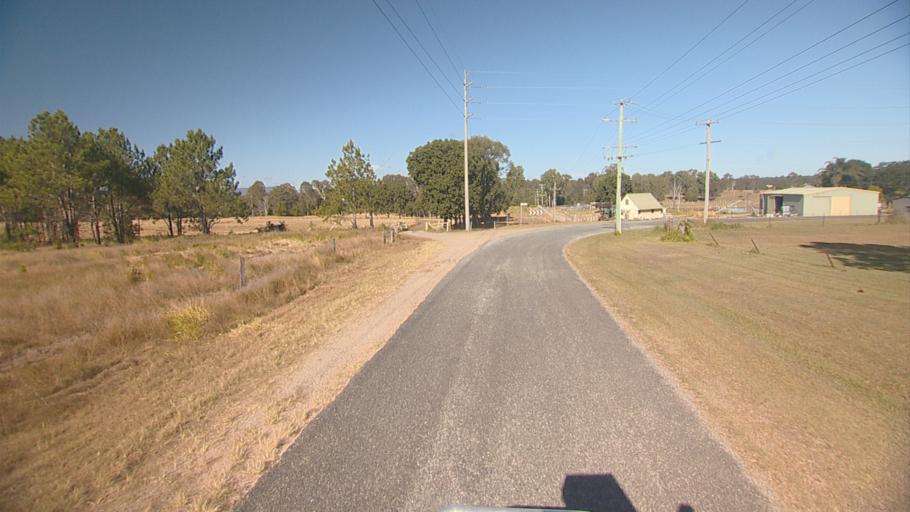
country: AU
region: Queensland
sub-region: Logan
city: Chambers Flat
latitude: -27.7628
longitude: 153.0906
